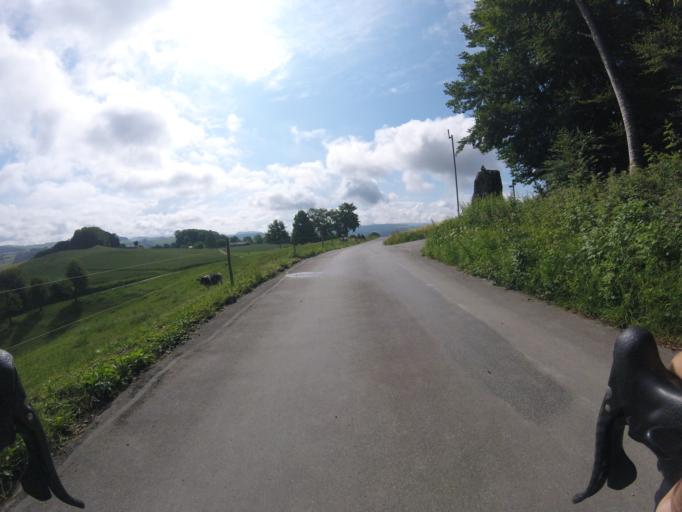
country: CH
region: Bern
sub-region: Bern-Mittelland District
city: Stettlen
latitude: 46.9403
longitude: 7.5371
